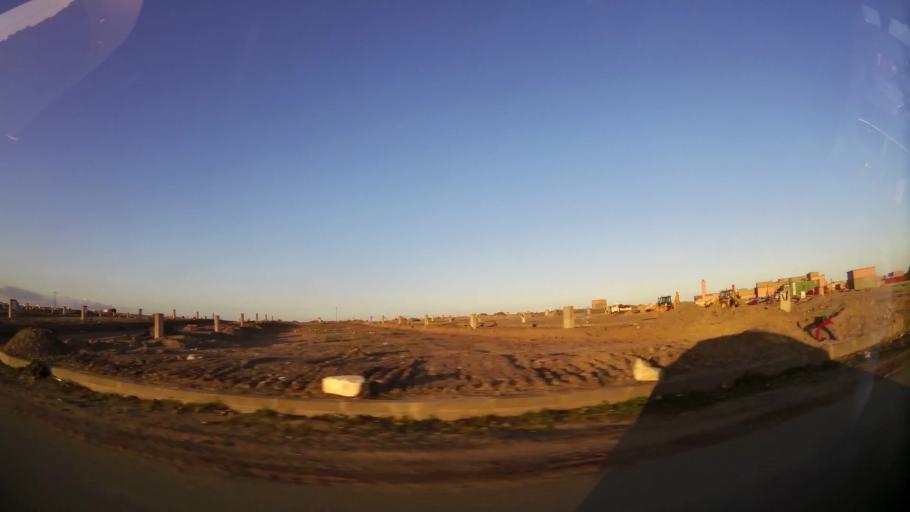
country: MA
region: Marrakech-Tensift-Al Haouz
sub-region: Kelaa-Des-Sraghna
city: Sidi Abdallah
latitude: 32.2408
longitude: -7.9367
